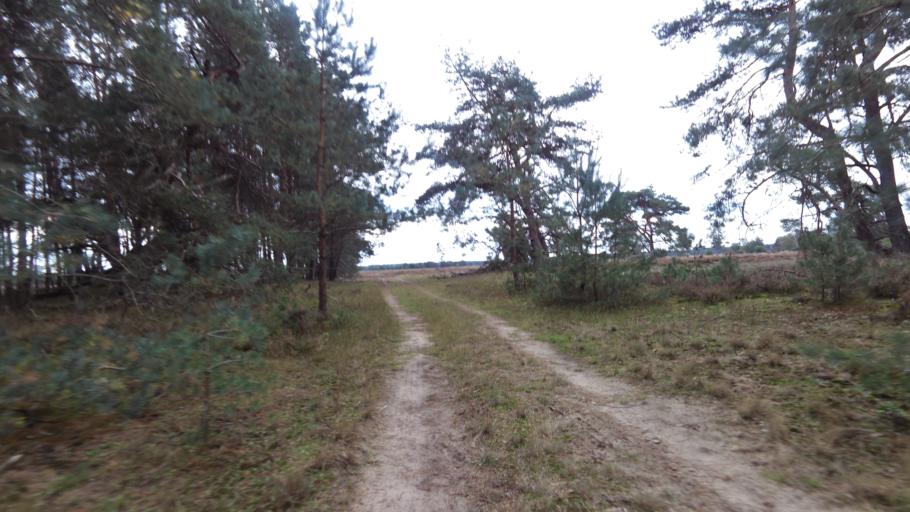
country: NL
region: Gelderland
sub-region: Gemeente Barneveld
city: Stroe
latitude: 52.1898
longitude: 5.7218
